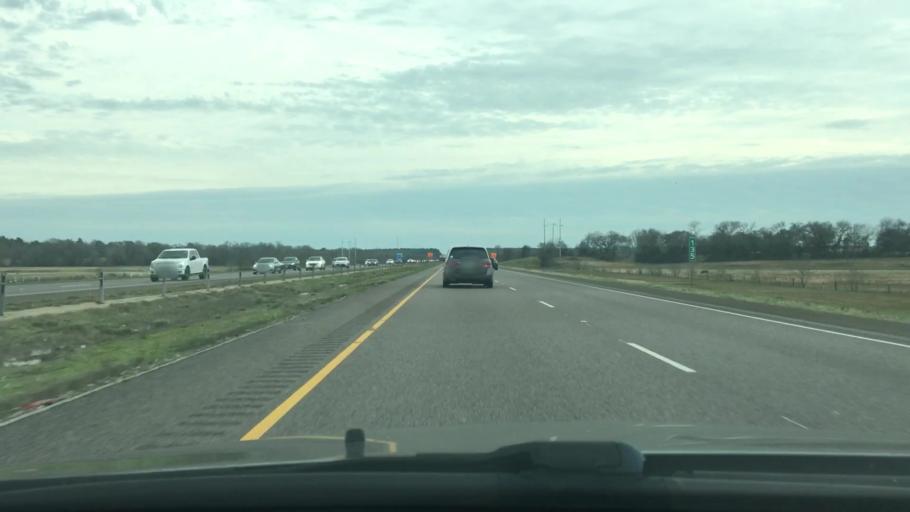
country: US
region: Texas
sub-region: Madison County
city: Madisonville
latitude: 30.9035
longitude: -95.7847
